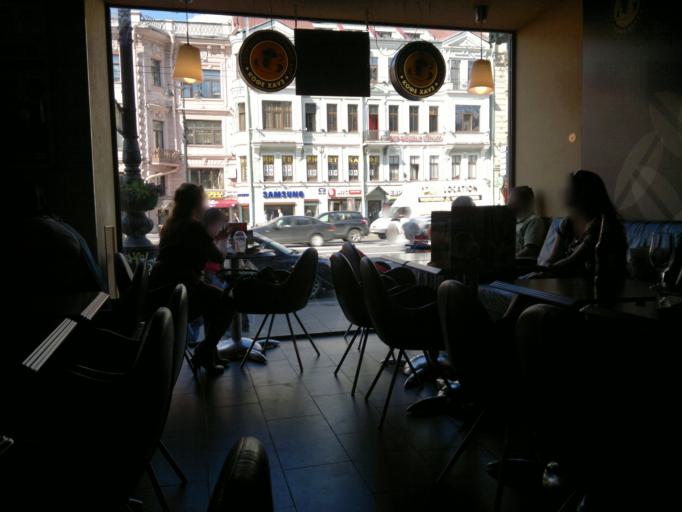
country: RU
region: St.-Petersburg
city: Centralniy
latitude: 59.9316
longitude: 30.3544
